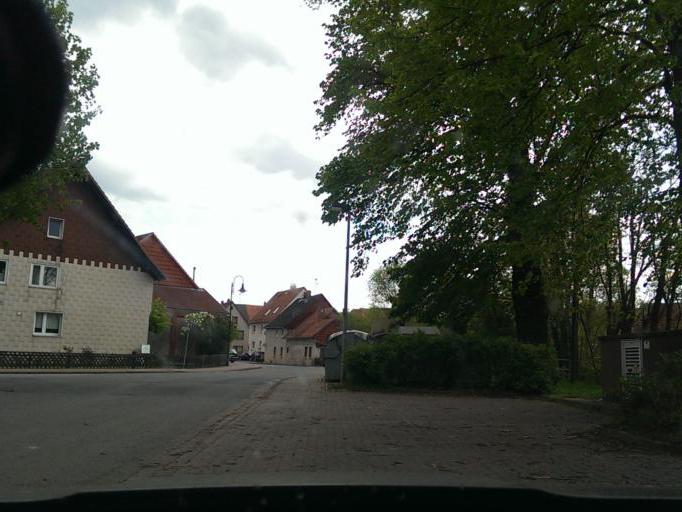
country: DE
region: Lower Saxony
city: Eime
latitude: 52.0794
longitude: 9.7214
